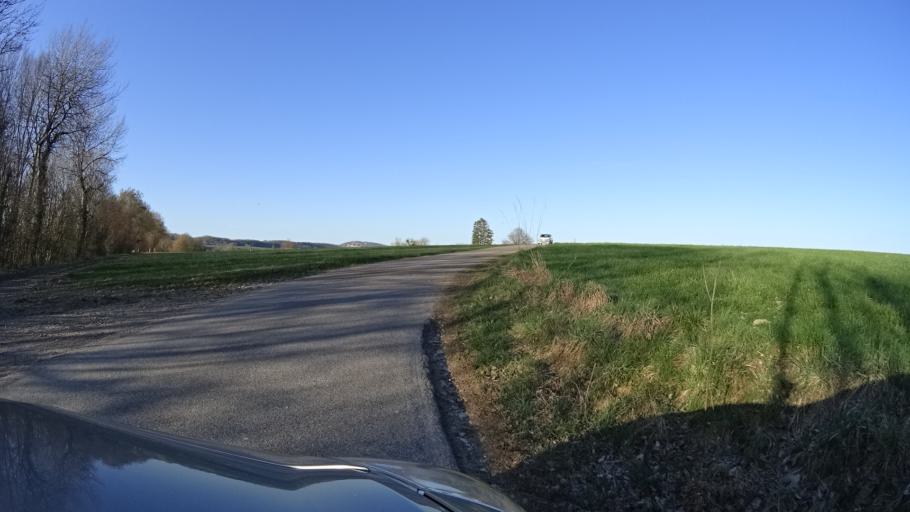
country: FR
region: Franche-Comte
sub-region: Departement du Doubs
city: Morre
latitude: 47.1939
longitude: 6.0543
